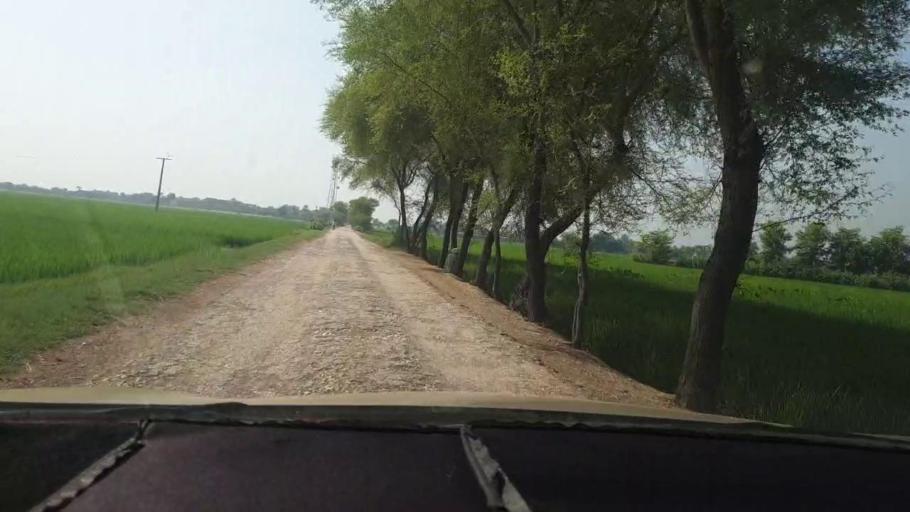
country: PK
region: Sindh
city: Kambar
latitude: 27.5637
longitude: 68.0579
